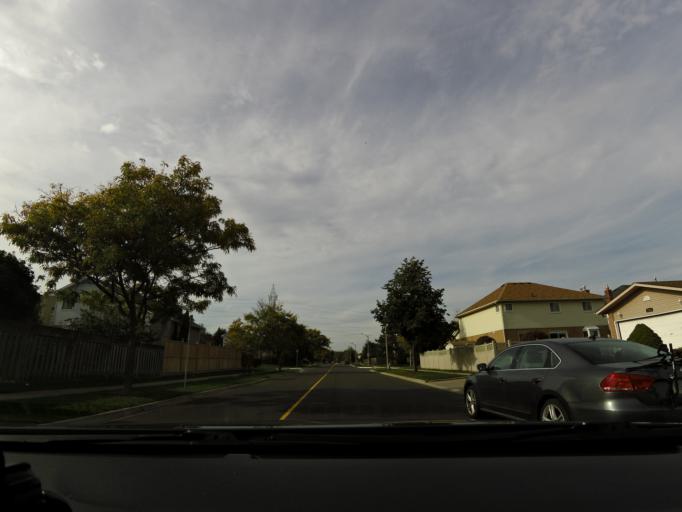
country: CA
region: Ontario
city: Burlington
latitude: 43.3827
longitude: -79.8162
